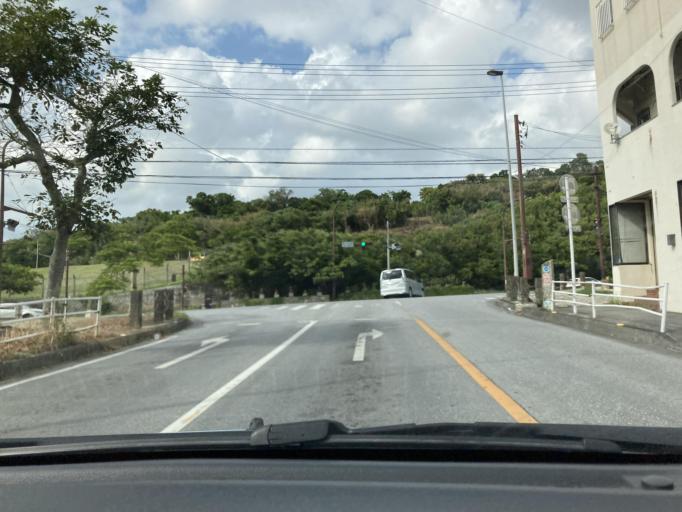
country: JP
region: Okinawa
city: Chatan
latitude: 26.2958
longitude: 127.7845
